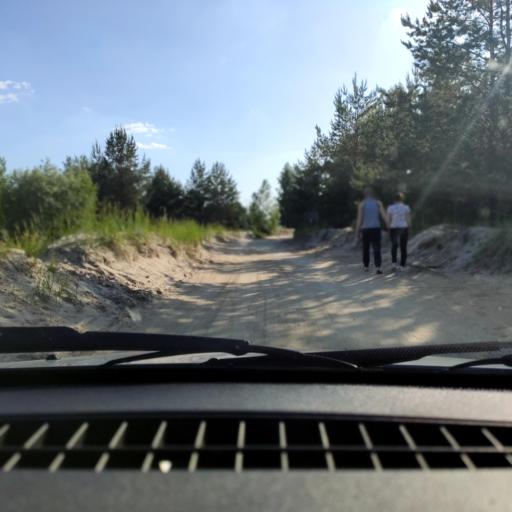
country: RU
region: Voronezj
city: Somovo
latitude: 51.7773
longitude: 39.2905
